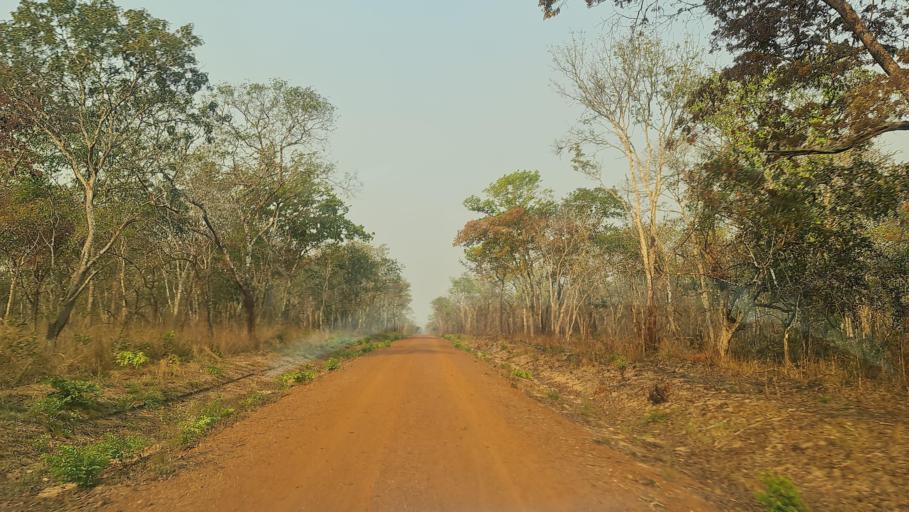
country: MZ
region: Zambezia
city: Quelimane
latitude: -17.1245
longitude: 37.1448
